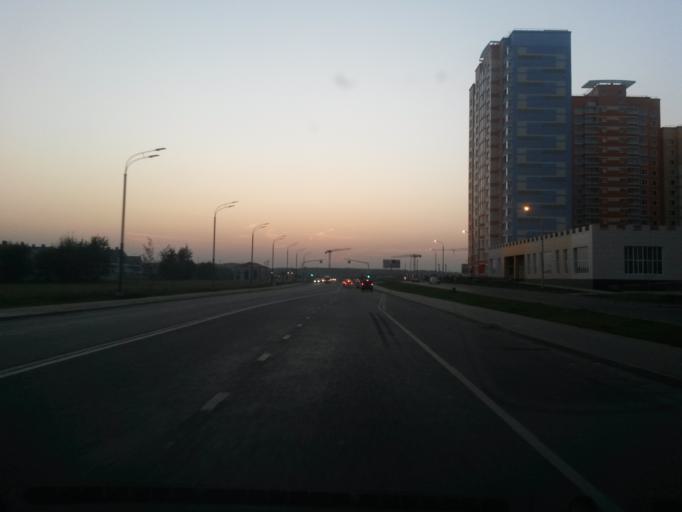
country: RU
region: Moskovskaya
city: Kommunarka
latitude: 55.5401
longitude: 37.4924
